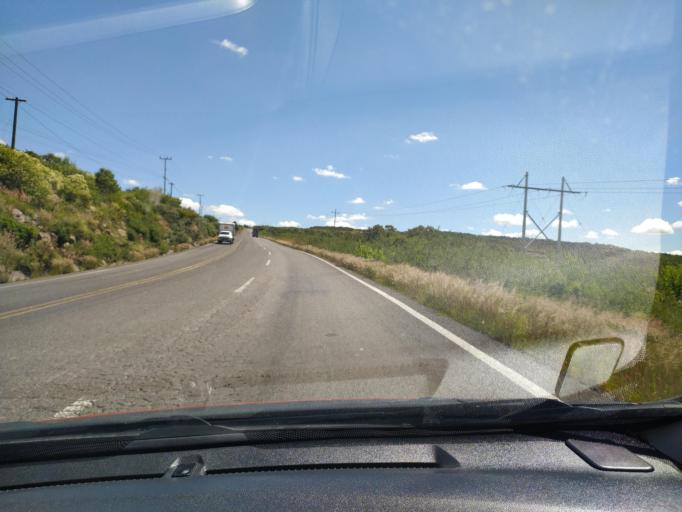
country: MX
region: Jalisco
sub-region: San Julian
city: Colonia Veintitres de Mayo
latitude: 21.0086
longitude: -102.2683
